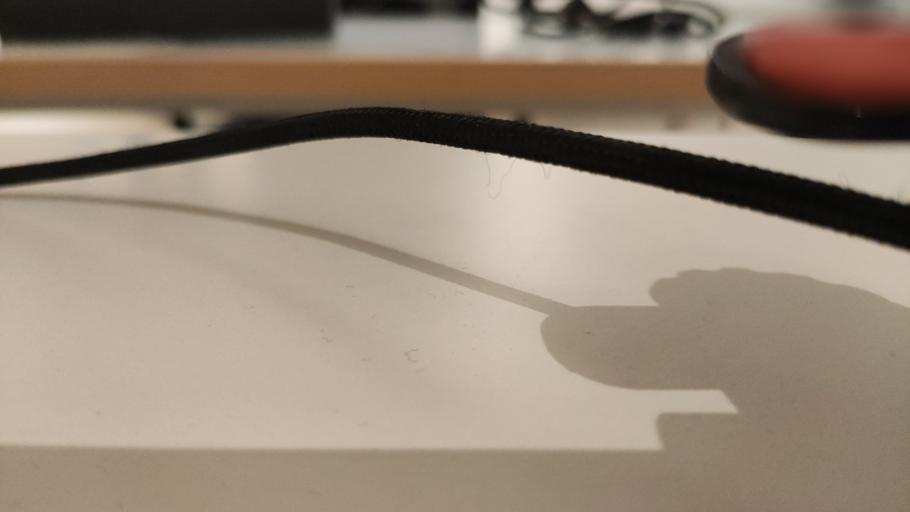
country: RU
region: Moskovskaya
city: Dorokhovo
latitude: 55.4470
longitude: 36.3520
